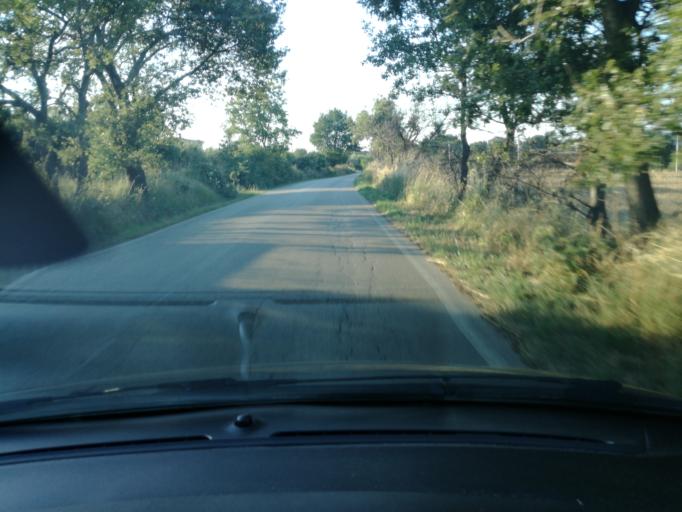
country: IT
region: Molise
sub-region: Provincia di Campobasso
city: San Giacomo degli Schiavoni
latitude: 41.9488
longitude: 14.9425
